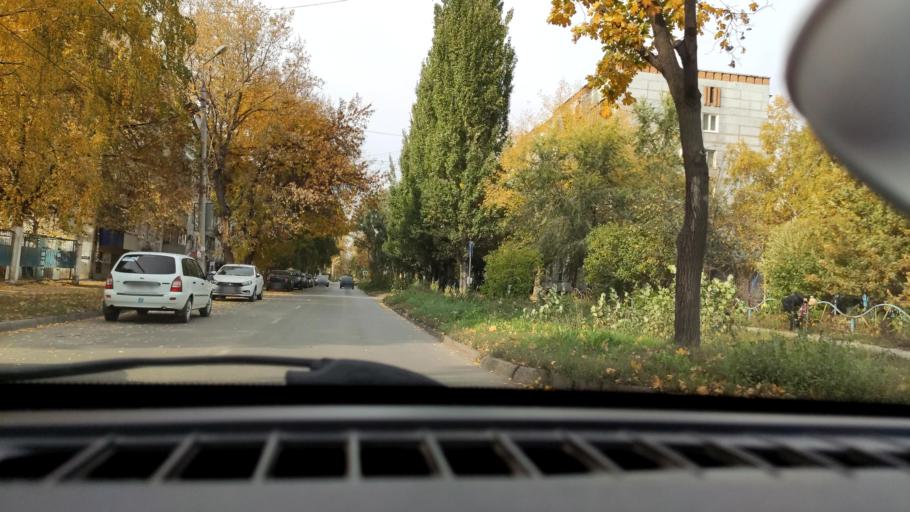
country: RU
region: Samara
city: Petra-Dubrava
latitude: 53.2248
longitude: 50.2694
